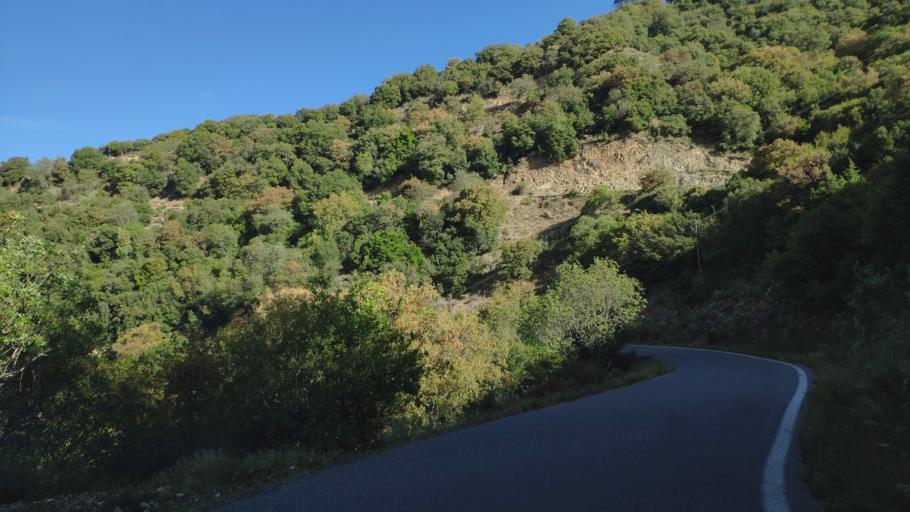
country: GR
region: Peloponnese
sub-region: Nomos Arkadias
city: Dimitsana
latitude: 37.5498
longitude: 22.0576
